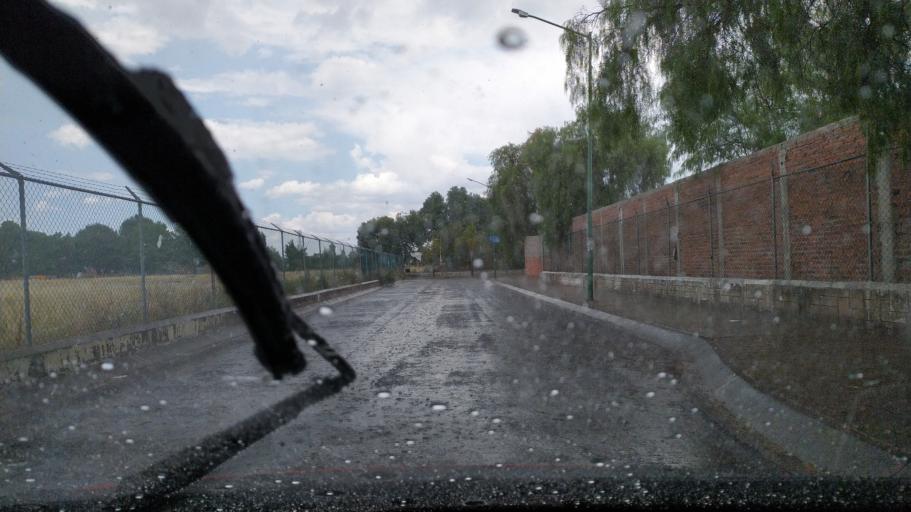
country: MX
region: Guanajuato
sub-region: San Francisco del Rincon
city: Estacion de San Francisco
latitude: 21.0311
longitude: -101.8295
